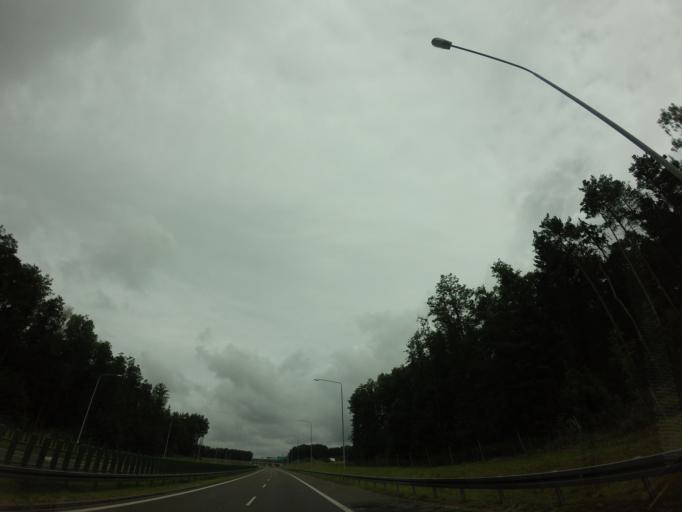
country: PL
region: West Pomeranian Voivodeship
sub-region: Powiat goleniowski
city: Przybiernow
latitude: 53.8308
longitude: 14.7508
